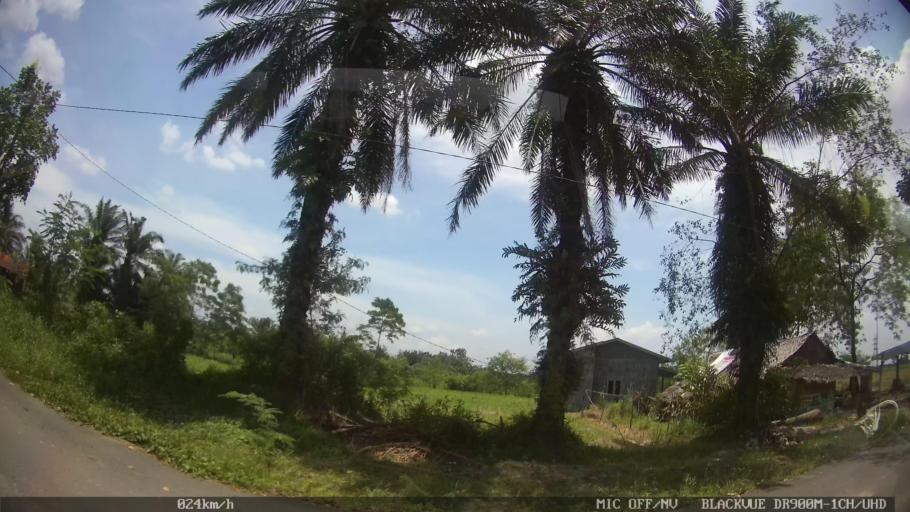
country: ID
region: North Sumatra
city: Binjai
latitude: 3.5913
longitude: 98.5252
